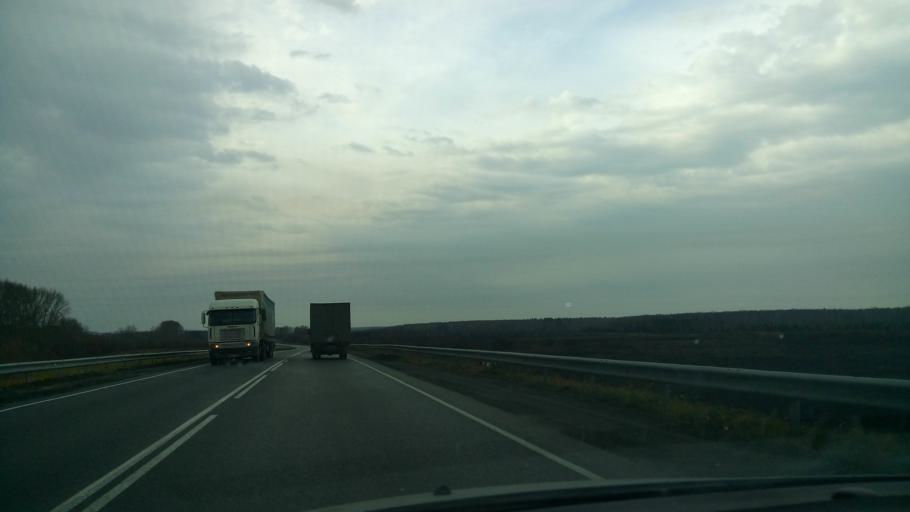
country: RU
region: Sverdlovsk
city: Obukhovskoye
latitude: 56.8397
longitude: 62.5824
